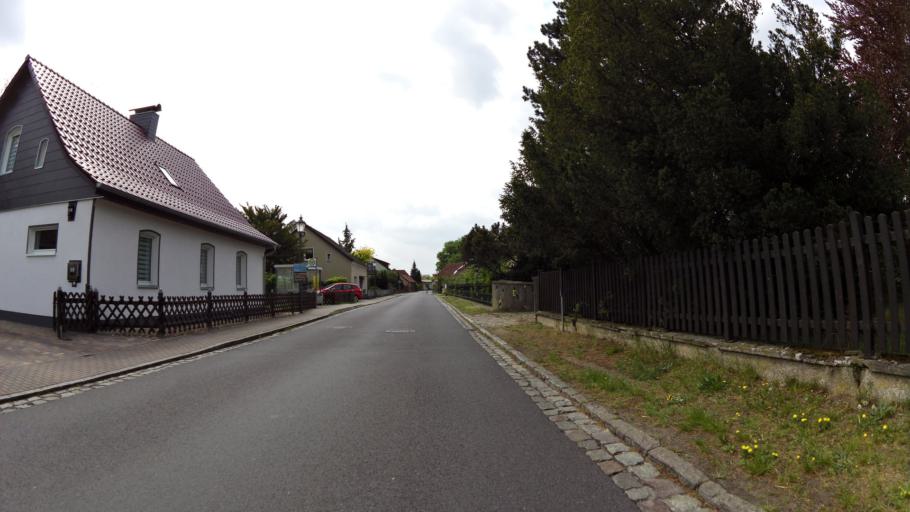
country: DE
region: Brandenburg
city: Bestensee
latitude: 52.2420
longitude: 13.7116
